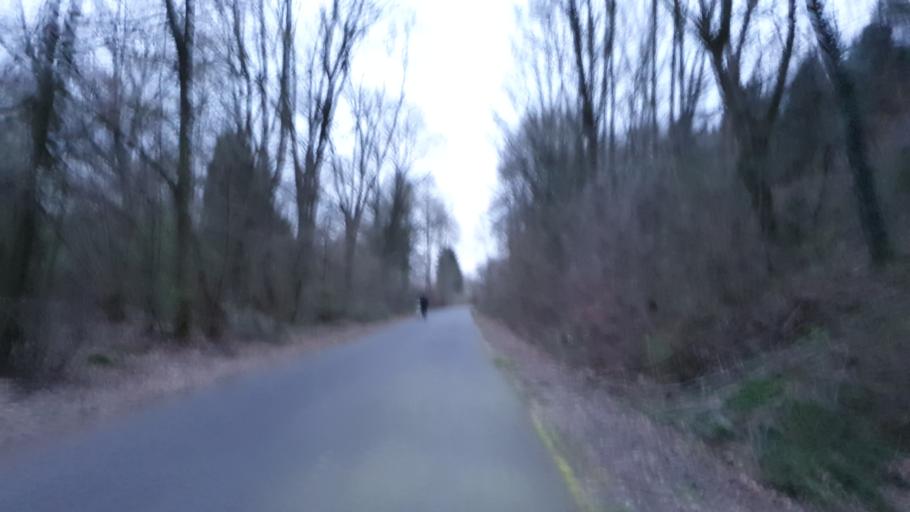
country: DE
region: North Rhine-Westphalia
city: Opladen
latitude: 51.0745
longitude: 7.0347
